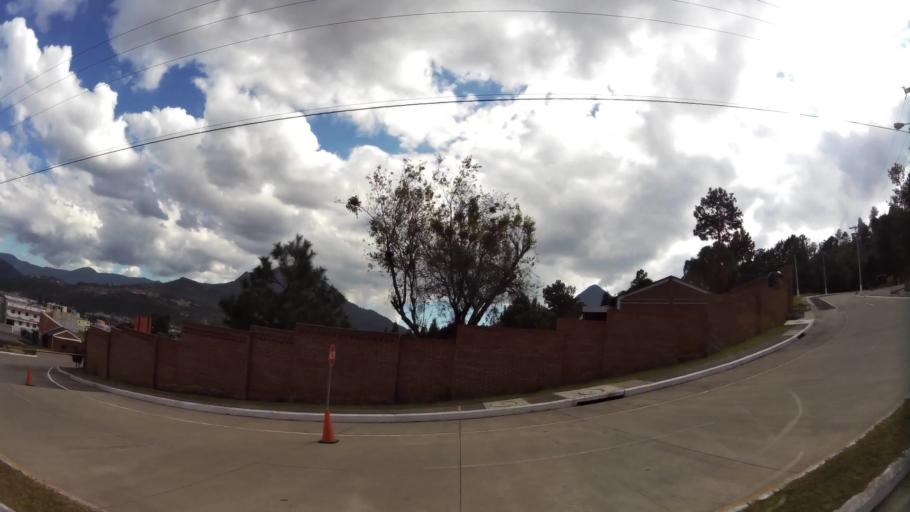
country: GT
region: Quetzaltenango
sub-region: Municipio de La Esperanza
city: La Esperanza
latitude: 14.8352
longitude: -91.5528
